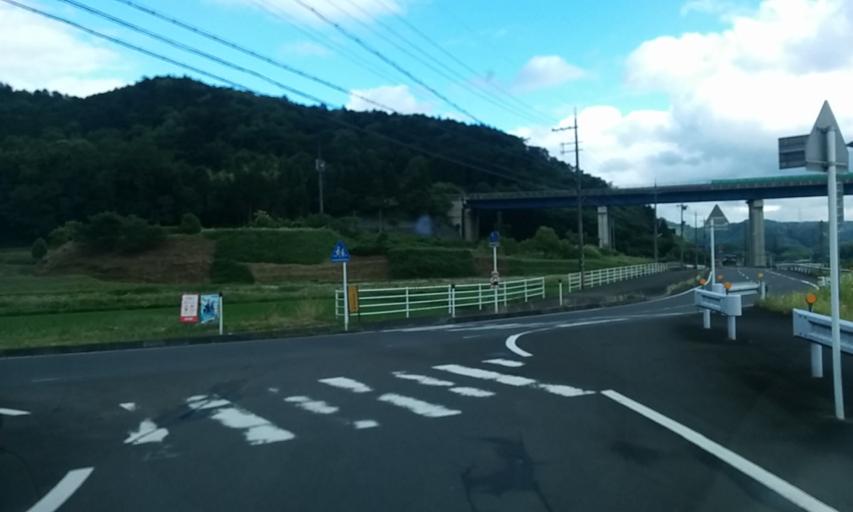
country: JP
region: Kyoto
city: Ayabe
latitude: 35.3492
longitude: 135.2877
